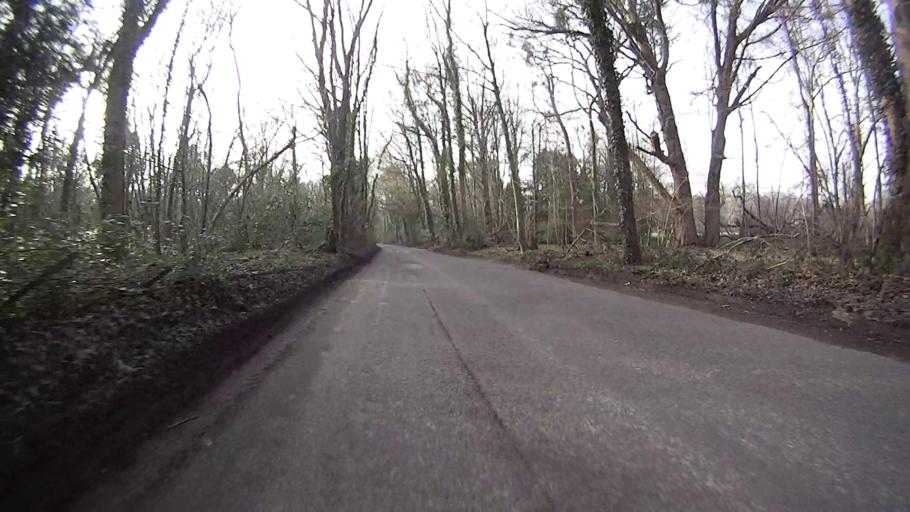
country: GB
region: England
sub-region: West Sussex
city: Copthorne
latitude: 51.1169
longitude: -0.1038
